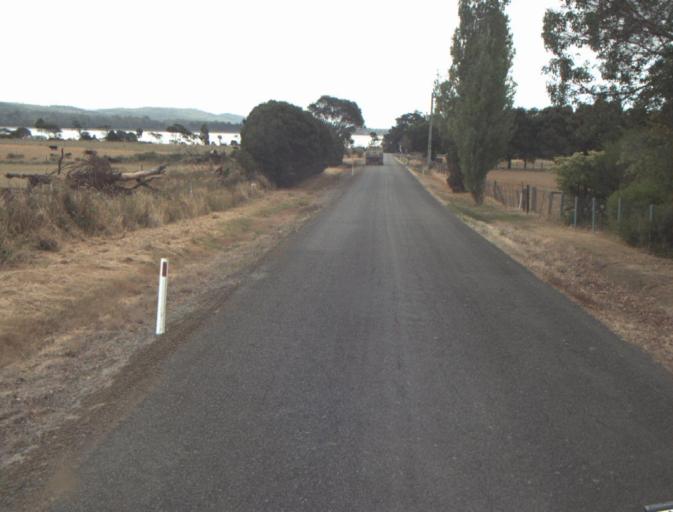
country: AU
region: Tasmania
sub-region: Launceston
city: Mayfield
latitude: -41.2887
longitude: 147.0014
